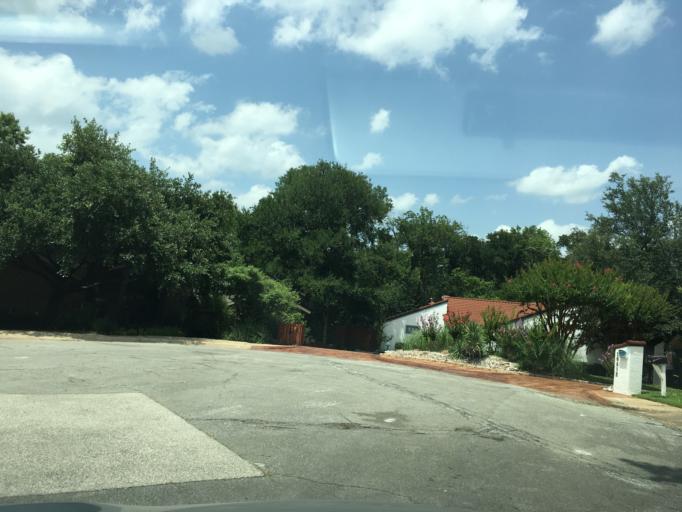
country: US
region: Texas
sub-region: Dallas County
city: University Park
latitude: 32.8941
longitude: -96.7762
